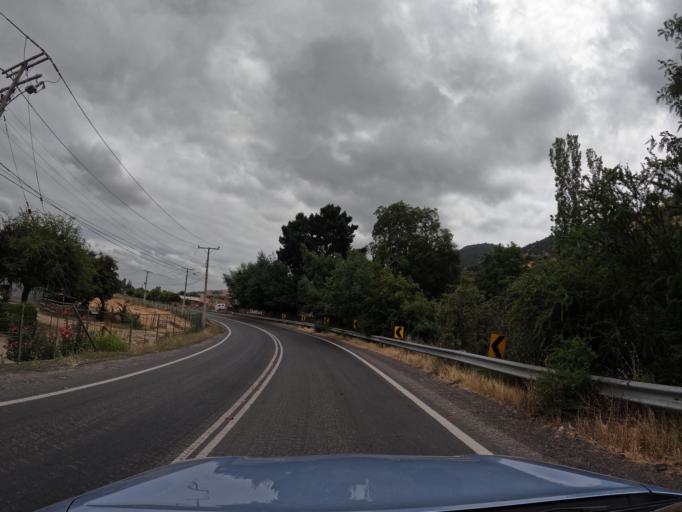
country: CL
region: Maule
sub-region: Provincia de Curico
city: Teno
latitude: -34.8092
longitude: -71.2152
